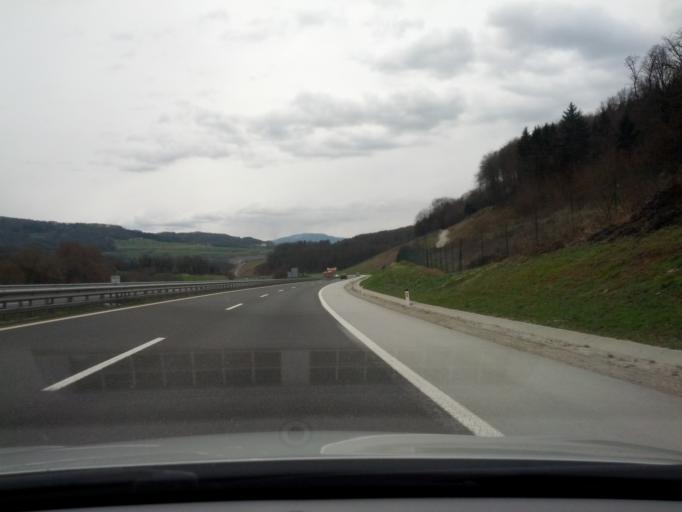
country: SI
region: Mirna Pec
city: Mirna Pec
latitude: 45.8725
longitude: 15.1095
